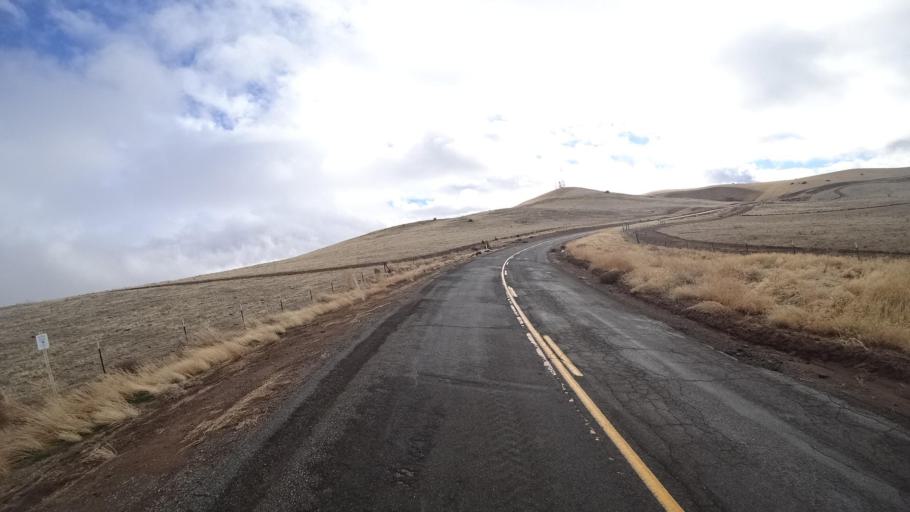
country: US
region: California
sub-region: Kern County
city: Maricopa
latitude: 34.9259
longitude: -119.4107
